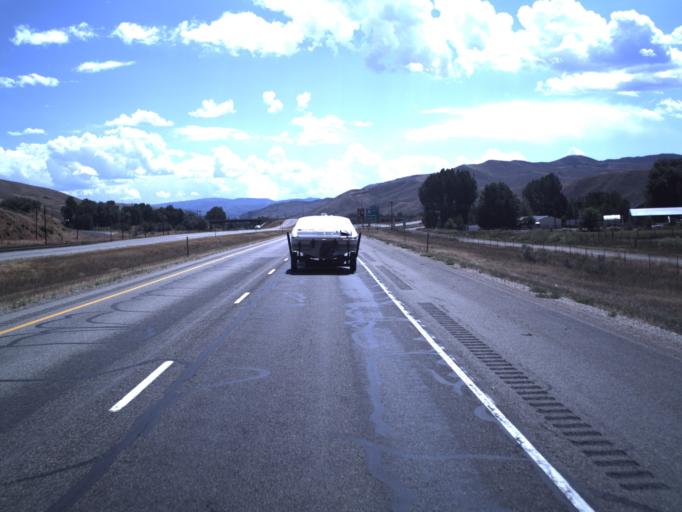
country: US
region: Utah
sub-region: Summit County
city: Coalville
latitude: 41.0218
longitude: -111.4945
